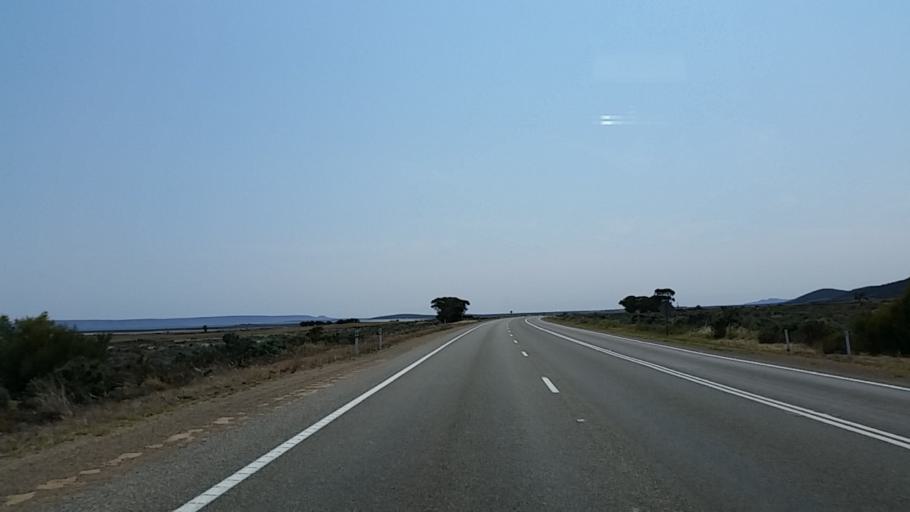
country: AU
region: South Australia
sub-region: Port Augusta
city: Port Augusta
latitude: -32.8045
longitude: 137.9632
